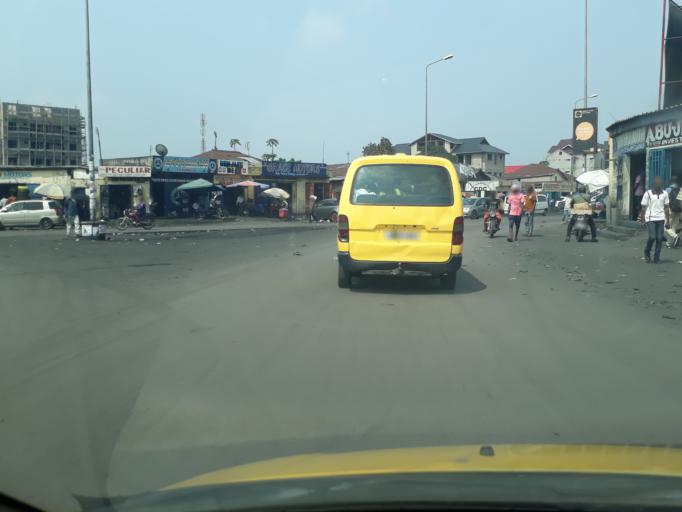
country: CD
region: Kinshasa
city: Kinshasa
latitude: -4.3397
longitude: 15.3096
